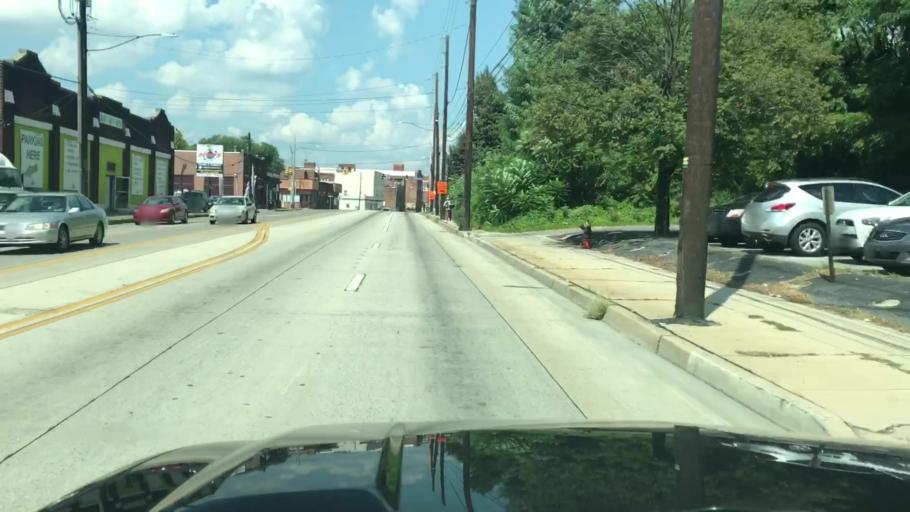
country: US
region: Pennsylvania
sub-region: Dauphin County
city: Harrisburg
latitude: 40.2634
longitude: -76.8739
